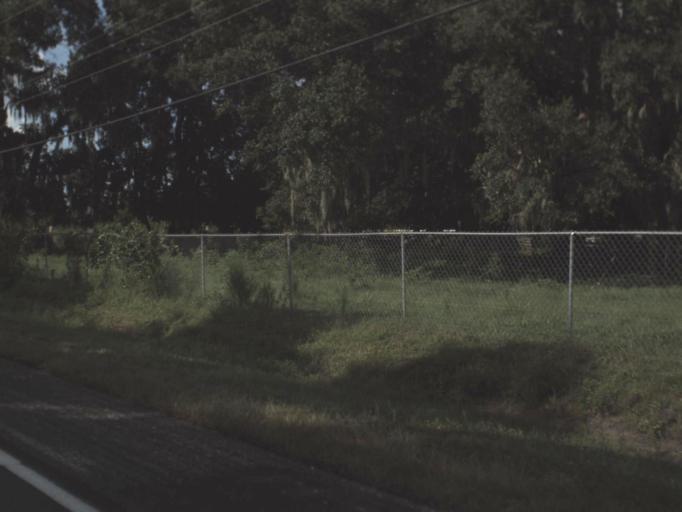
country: US
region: Florida
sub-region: Polk County
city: Combee Settlement
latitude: 28.0959
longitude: -81.9056
